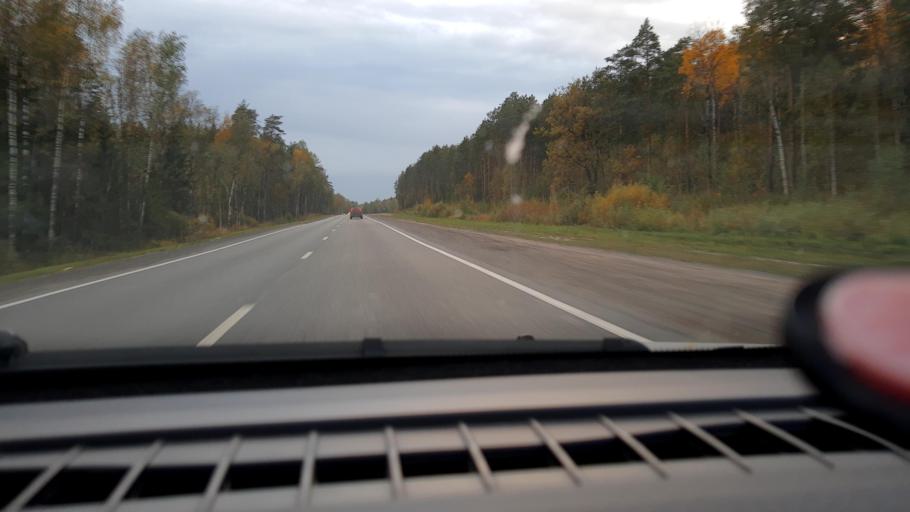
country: RU
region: Vladimir
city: Kameshkovo
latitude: 56.1937
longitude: 40.9404
